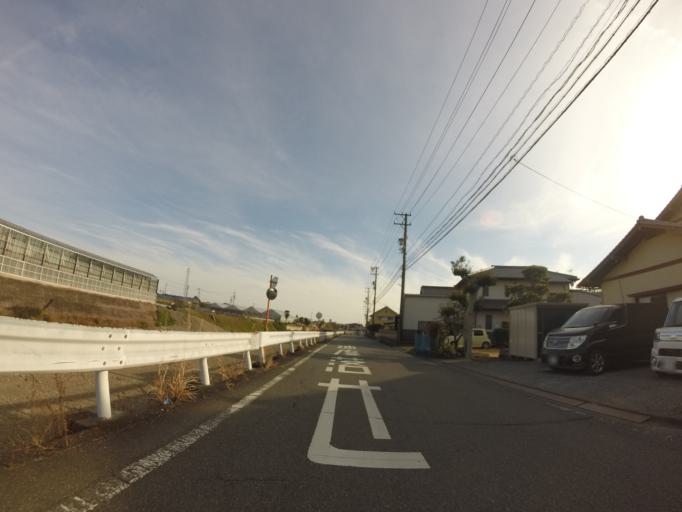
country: JP
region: Shizuoka
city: Shizuoka-shi
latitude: 35.0585
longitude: 138.4730
